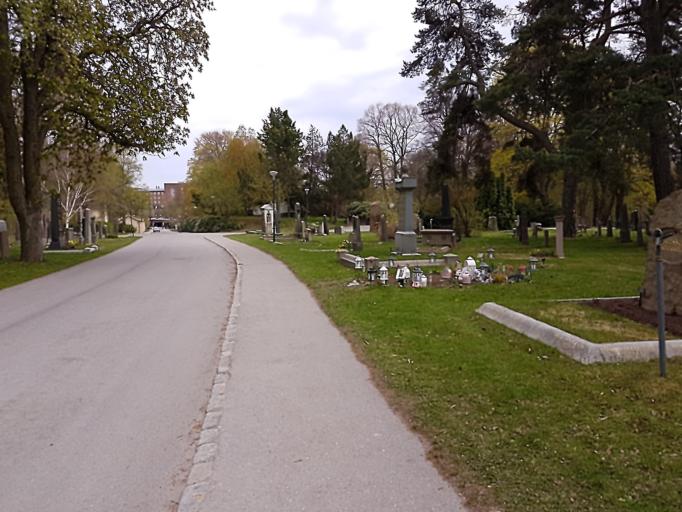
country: SE
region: Stockholm
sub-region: Norrtalje Kommun
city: Bergshamra
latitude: 59.3559
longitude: 18.0278
